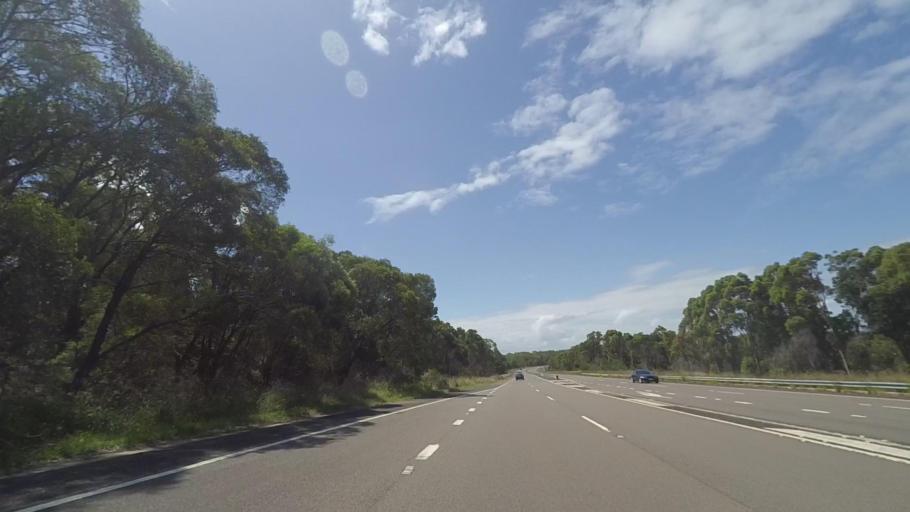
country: AU
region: New South Wales
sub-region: Wyong Shire
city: Kingfisher Shores
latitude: -33.1428
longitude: 151.6102
